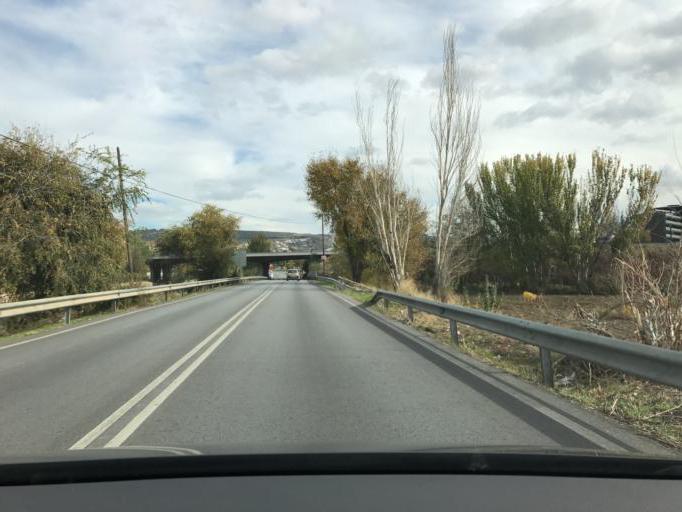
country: ES
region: Andalusia
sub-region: Provincia de Granada
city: Armilla
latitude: 37.1618
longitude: -3.6124
